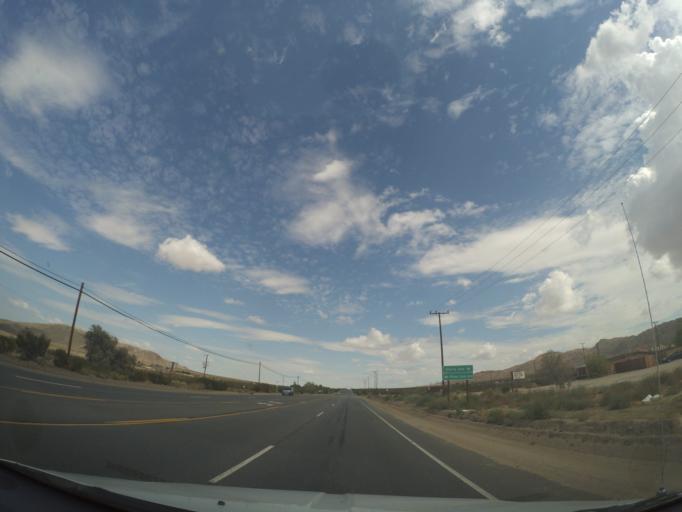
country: US
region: California
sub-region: San Bernardino County
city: Joshua Tree
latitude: 34.1351
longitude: -116.2247
